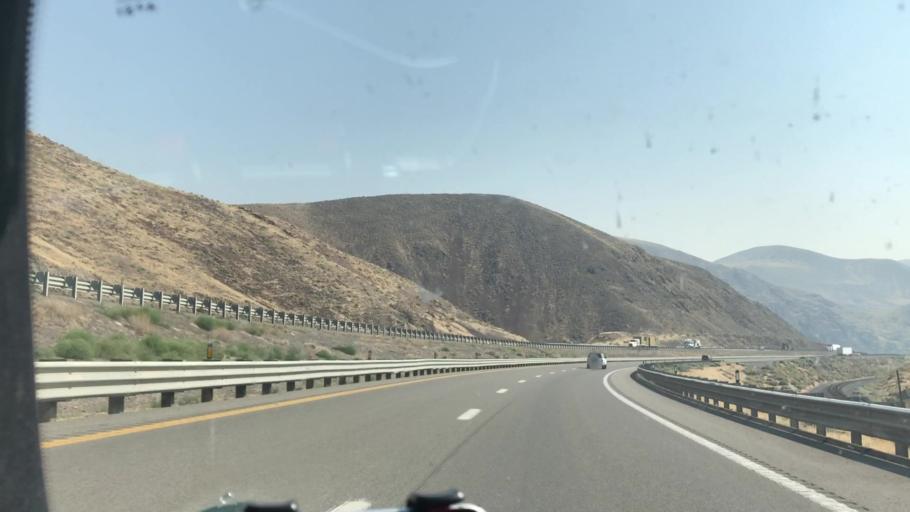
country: US
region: Nevada
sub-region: Lyon County
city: Fernley
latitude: 39.5841
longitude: -119.4691
